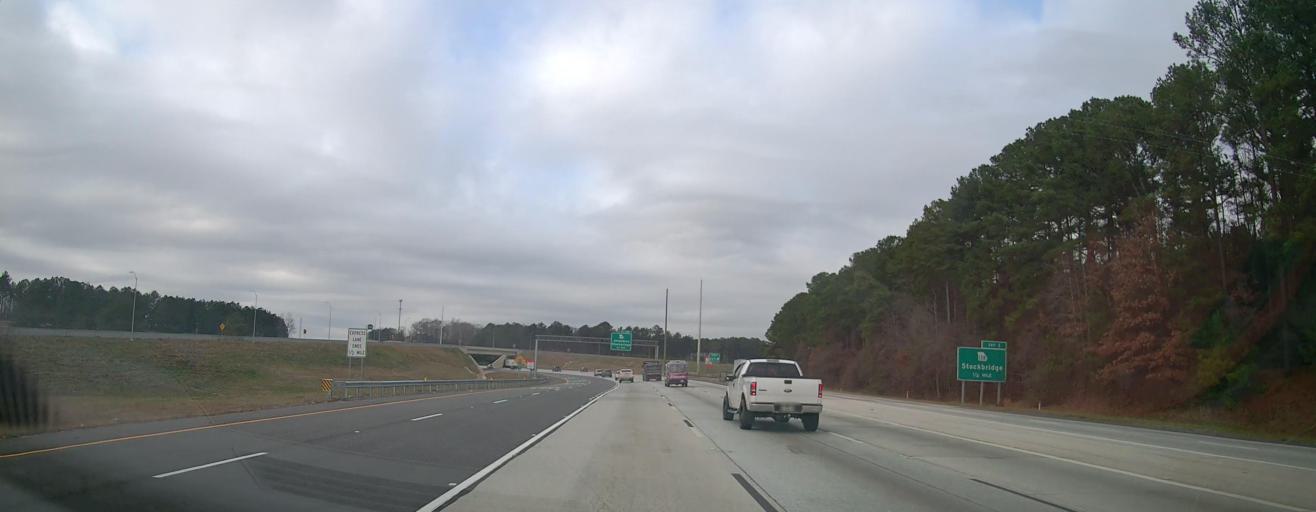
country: US
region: Georgia
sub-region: Henry County
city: Stockbridge
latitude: 33.5423
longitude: -84.2656
